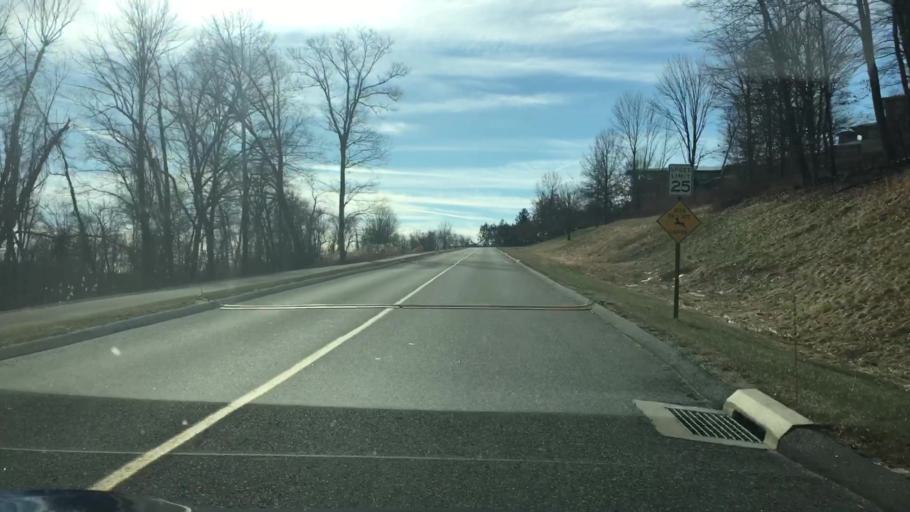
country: US
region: Connecticut
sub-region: Fairfield County
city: Danbury
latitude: 41.3757
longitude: -73.5115
